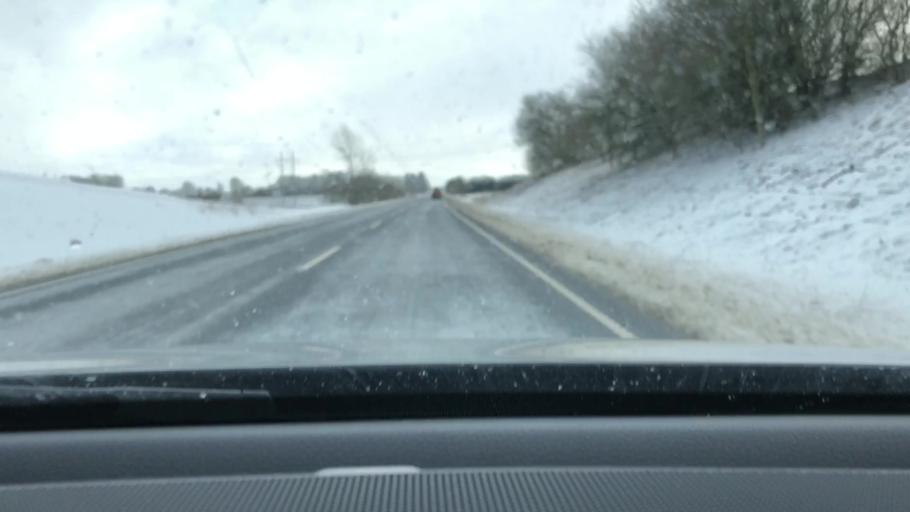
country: DK
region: Central Jutland
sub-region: Favrskov Kommune
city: Hammel
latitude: 56.1950
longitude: 9.8493
